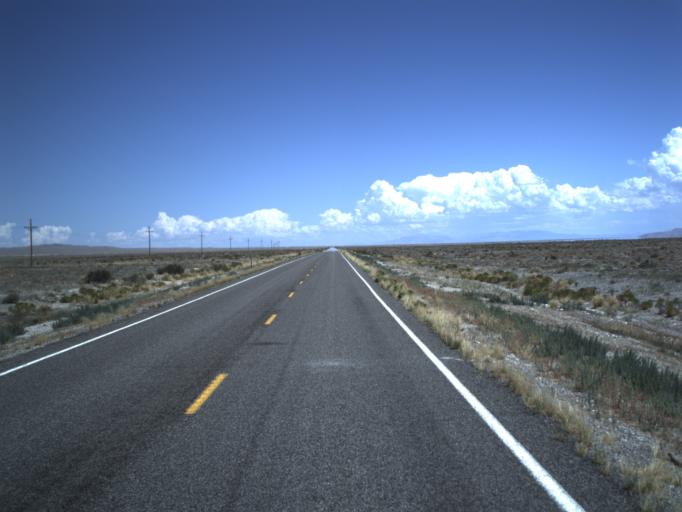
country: US
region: Utah
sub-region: Millard County
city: Delta
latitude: 39.0865
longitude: -113.1826
